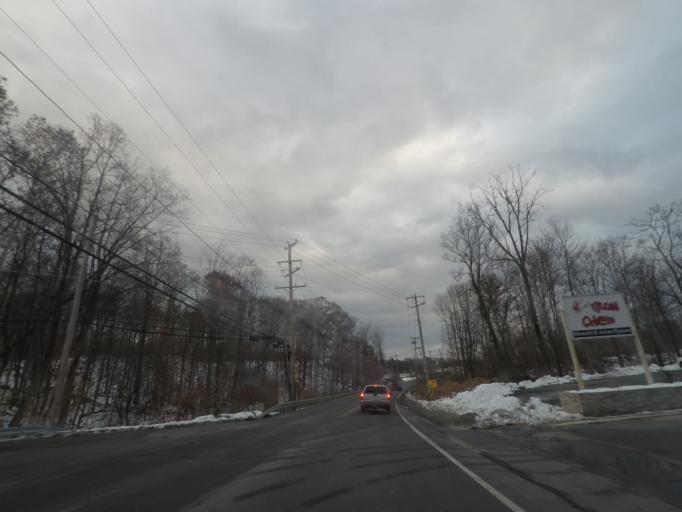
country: US
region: New York
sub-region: Orange County
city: Balmville
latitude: 41.5299
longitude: -74.0358
